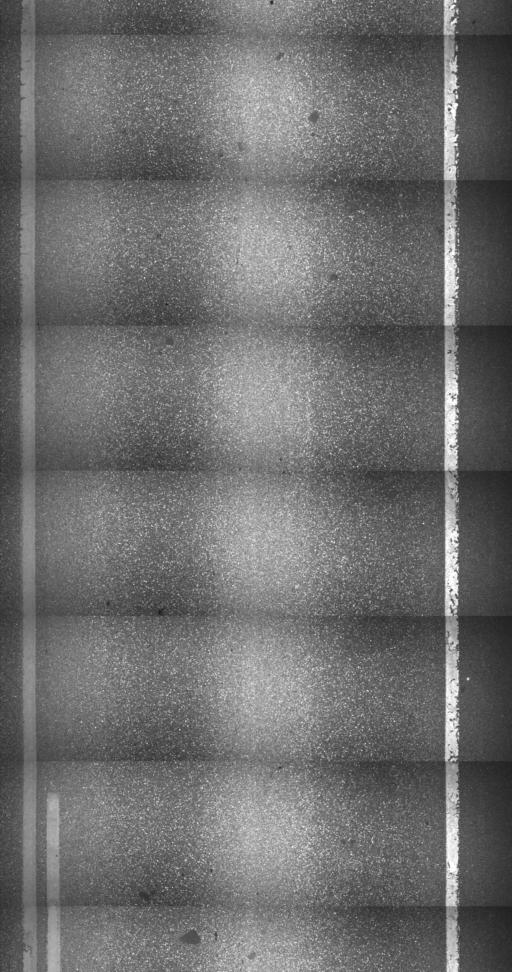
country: US
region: Vermont
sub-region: Chittenden County
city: Hinesburg
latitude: 44.2802
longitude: -73.0684
